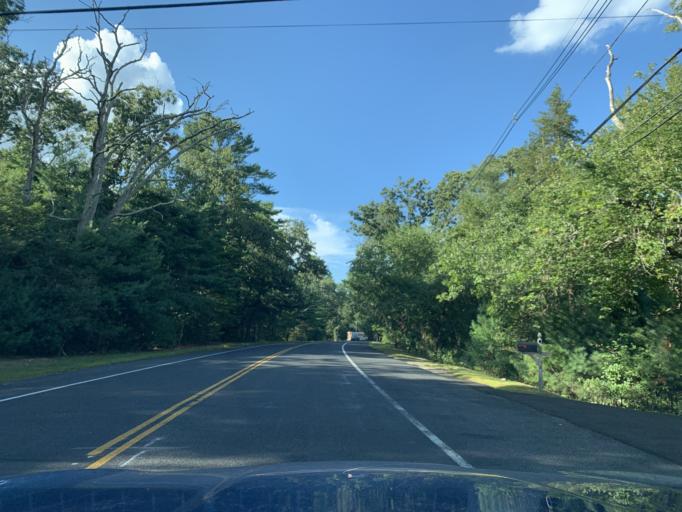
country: US
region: Rhode Island
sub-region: Washington County
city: Charlestown
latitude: 41.4640
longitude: -71.6195
